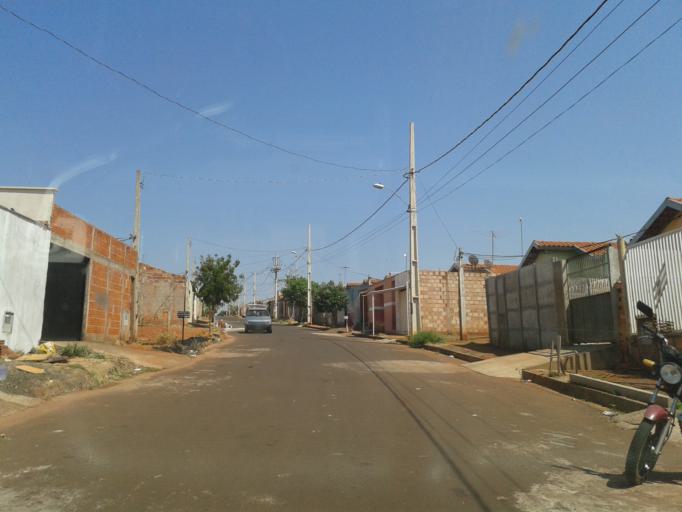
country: BR
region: Minas Gerais
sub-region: Ituiutaba
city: Ituiutaba
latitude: -19.0158
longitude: -49.4536
